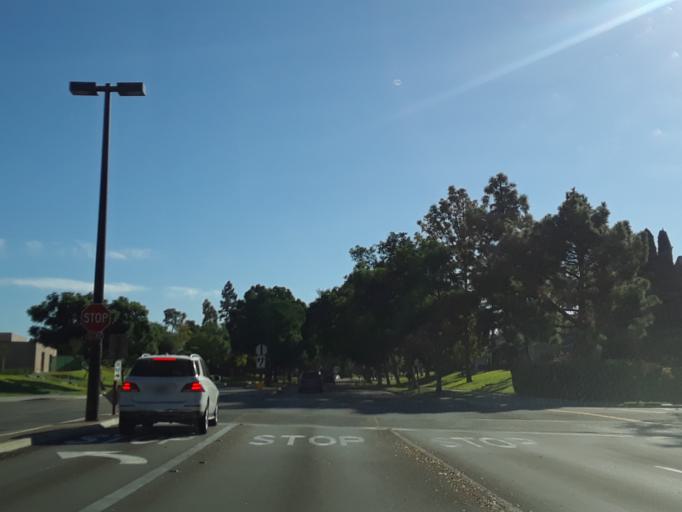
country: US
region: California
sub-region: Orange County
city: Irvine
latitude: 33.6859
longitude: -117.8030
